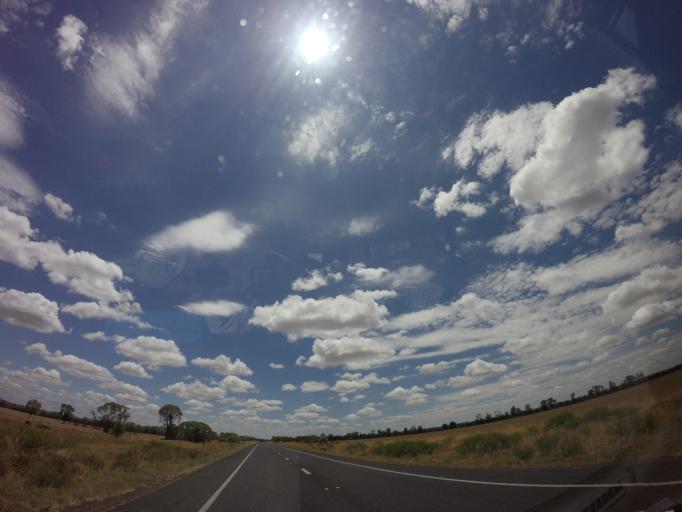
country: AU
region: New South Wales
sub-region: Moree Plains
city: Boggabilla
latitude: -28.8793
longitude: 150.1635
